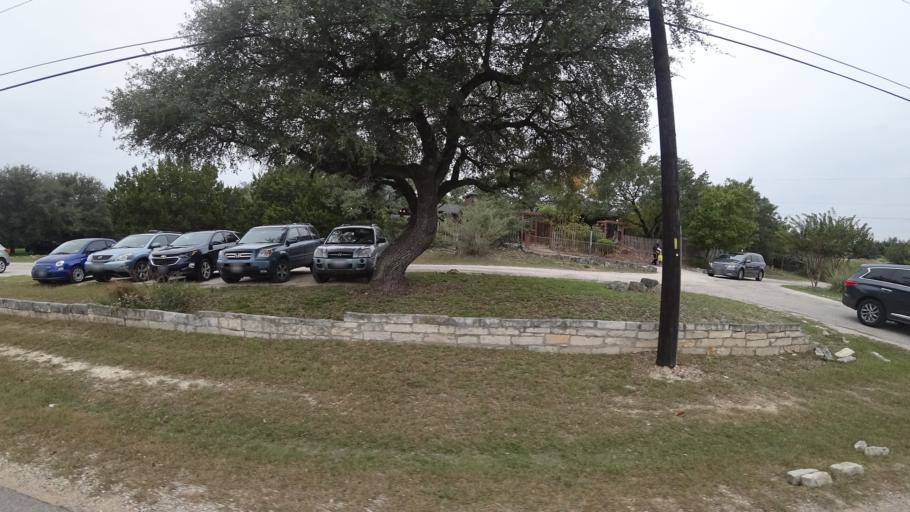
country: US
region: Texas
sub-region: Travis County
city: Lakeway
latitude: 30.3735
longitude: -97.9381
